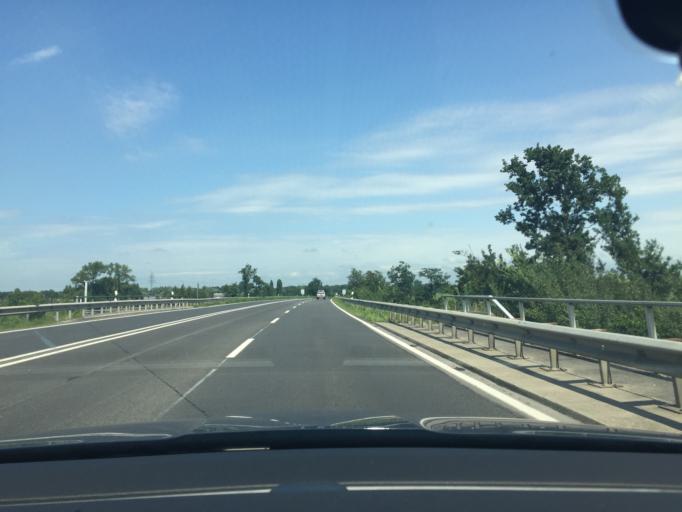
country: DE
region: Lower Saxony
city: Filsum
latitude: 53.2268
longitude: 7.6396
